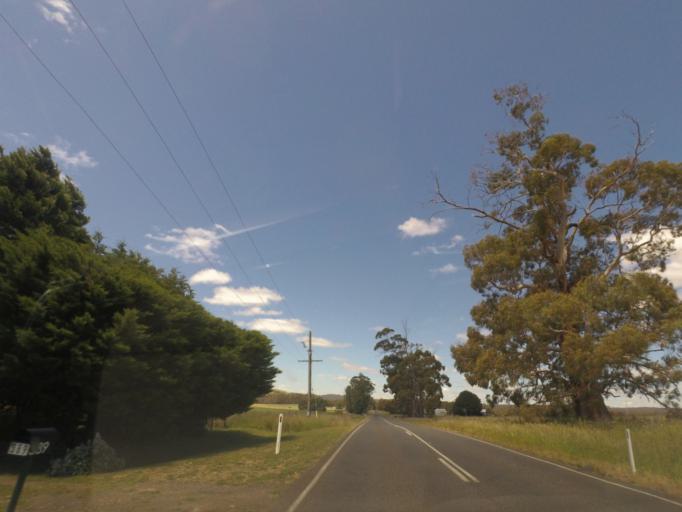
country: AU
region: Victoria
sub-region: Mount Alexander
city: Castlemaine
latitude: -37.3211
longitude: 144.2024
